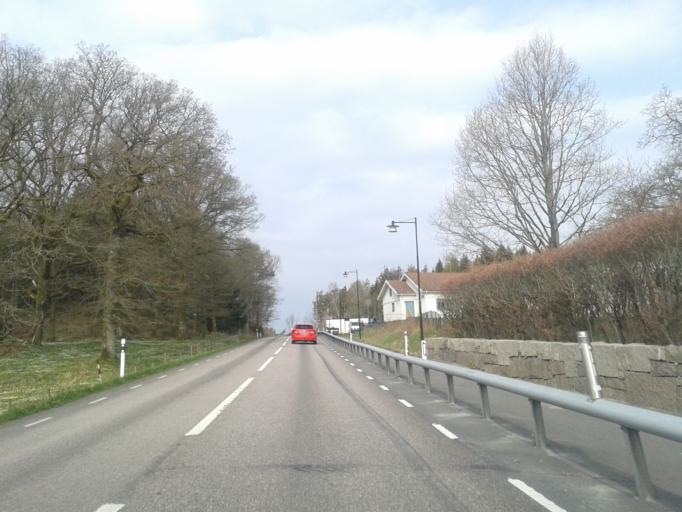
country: SE
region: Vaestra Goetaland
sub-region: Kungalvs Kommun
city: Kode
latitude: 57.8954
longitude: 11.8267
